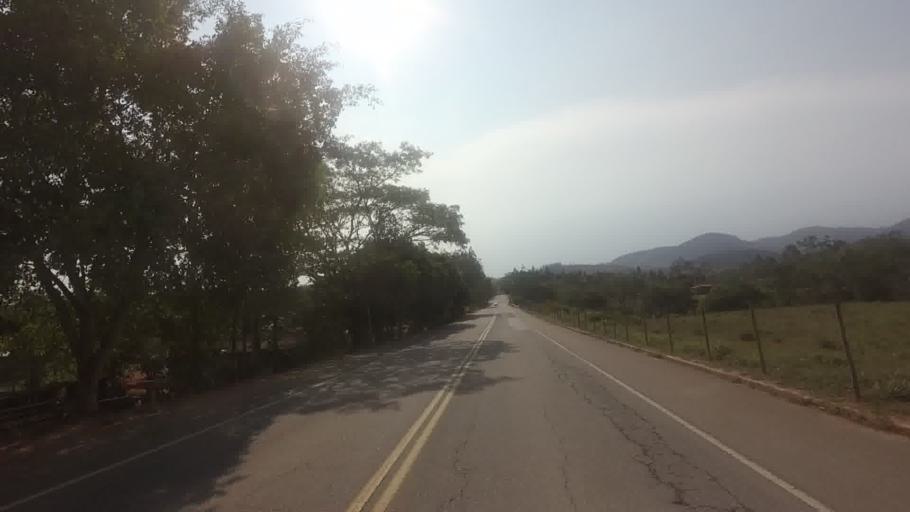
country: BR
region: Rio de Janeiro
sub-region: Bom Jesus Do Itabapoana
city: Bom Jesus do Itabapoana
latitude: -21.1364
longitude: -41.6405
